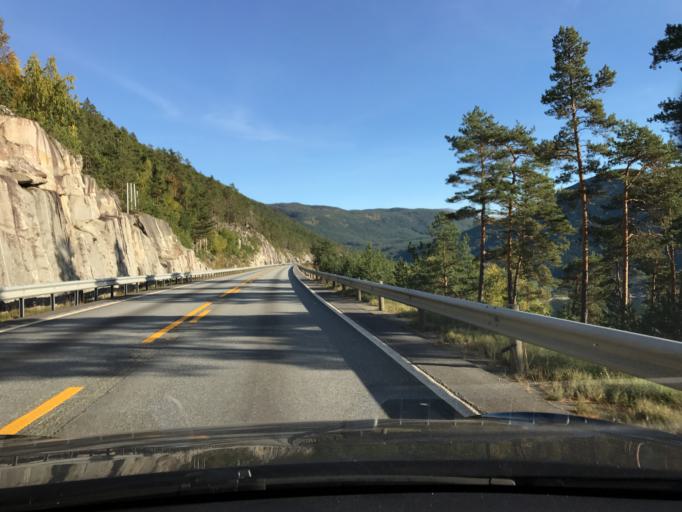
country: NO
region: Sogn og Fjordane
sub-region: Sogndal
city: Sogndalsfjora
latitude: 61.1881
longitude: 7.2381
